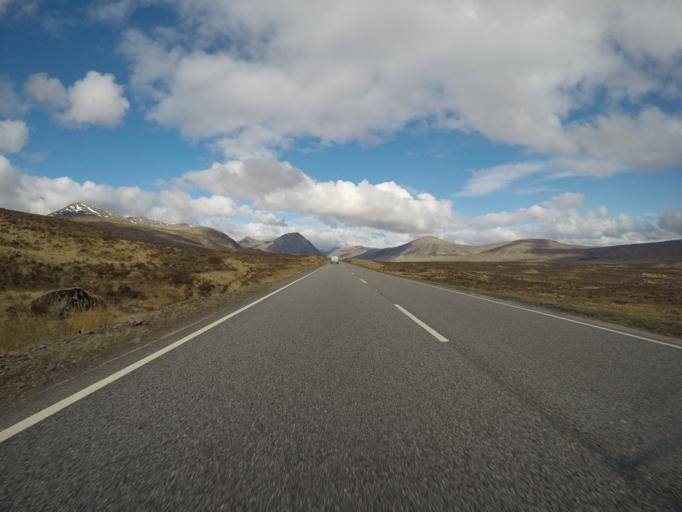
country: GB
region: Scotland
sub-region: Highland
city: Spean Bridge
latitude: 56.6297
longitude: -4.7786
